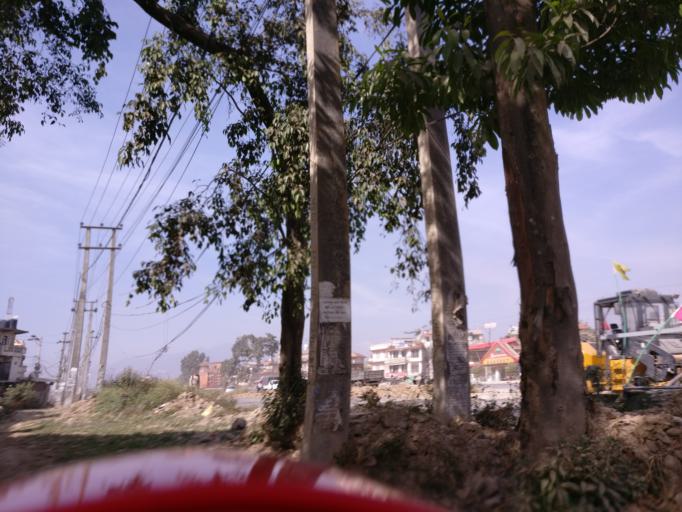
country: NP
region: Central Region
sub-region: Bagmati Zone
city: Patan
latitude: 27.6633
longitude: 85.3154
